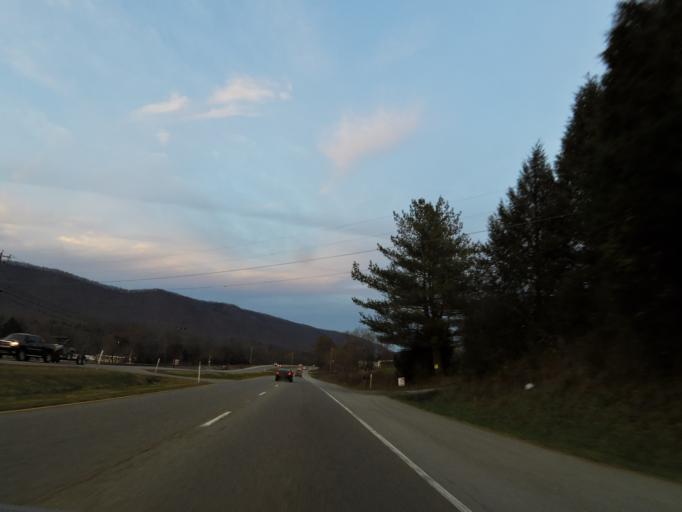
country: US
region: Tennessee
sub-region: Roane County
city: Midtown
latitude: 35.8993
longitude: -84.6045
